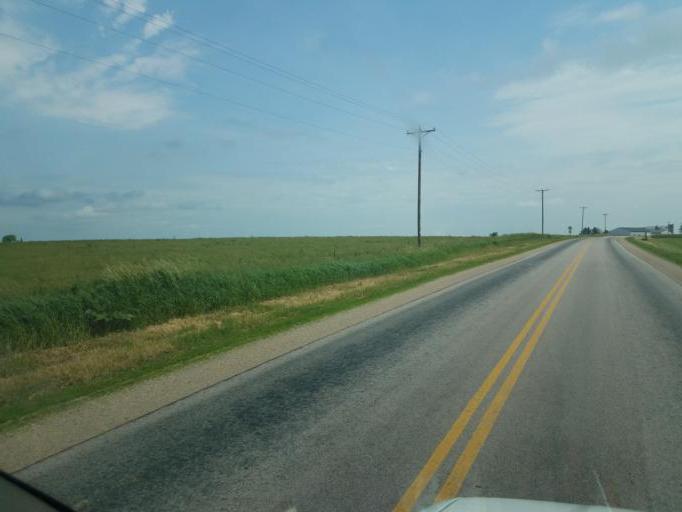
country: US
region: Wisconsin
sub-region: Monroe County
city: Cashton
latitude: 43.7562
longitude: -90.7481
